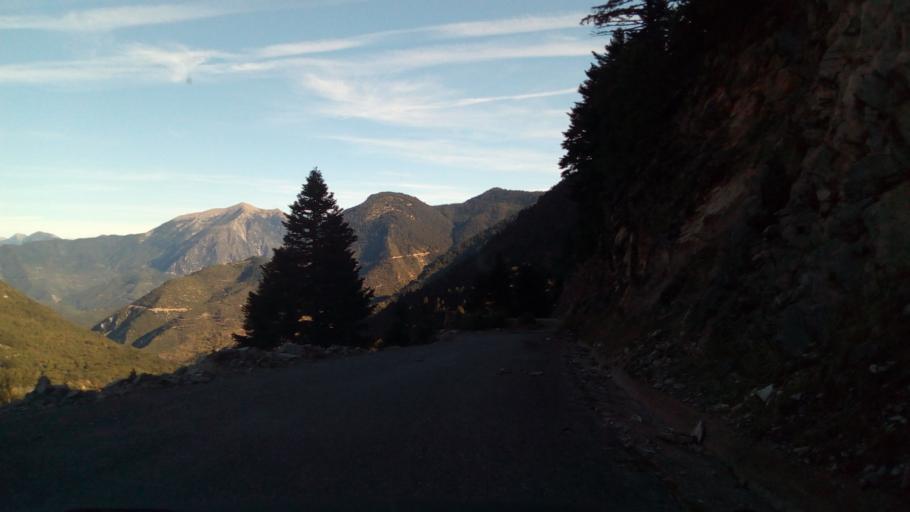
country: GR
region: West Greece
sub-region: Nomos Aitolias kai Akarnanias
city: Nafpaktos
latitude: 38.5384
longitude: 21.8495
